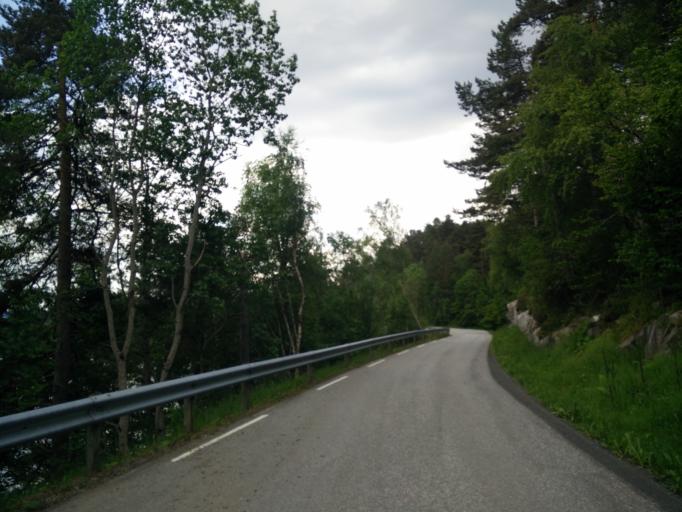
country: NO
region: More og Romsdal
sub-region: Kristiansund
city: Rensvik
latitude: 63.0272
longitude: 7.9535
